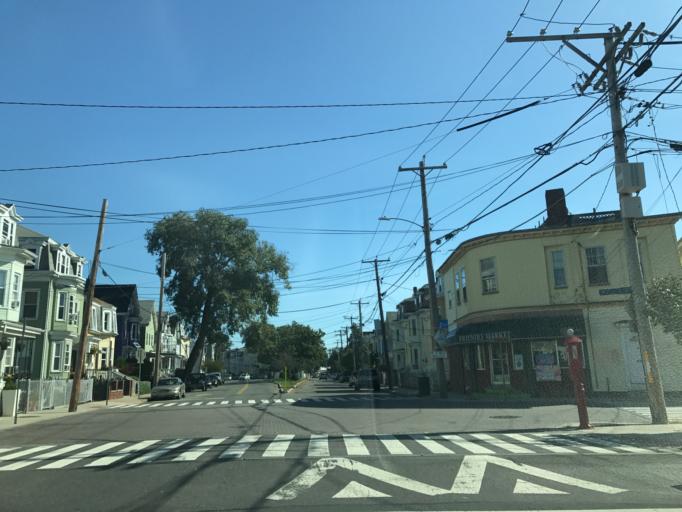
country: US
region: Massachusetts
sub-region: Middlesex County
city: Cambridge
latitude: 42.3765
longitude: -71.0998
